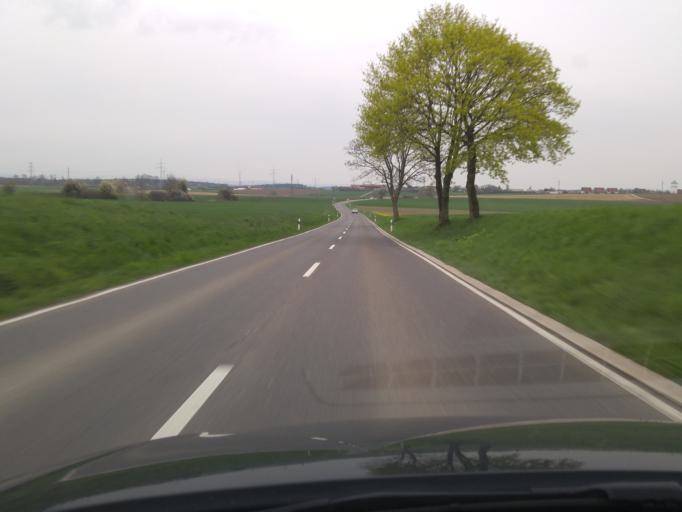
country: DE
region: Baden-Wuerttemberg
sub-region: Karlsruhe Region
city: Huffenhardt
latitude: 49.2835
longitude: 9.0857
